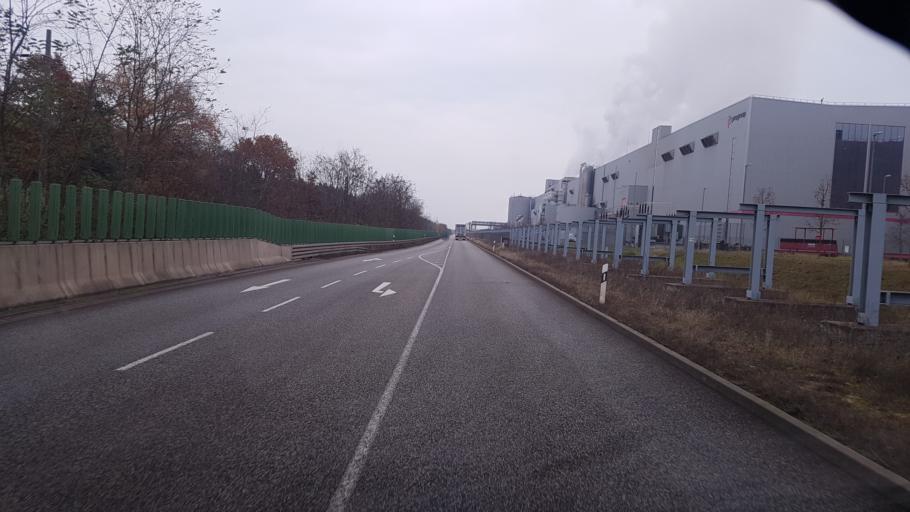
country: DE
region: Brandenburg
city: Ziltendorf
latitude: 52.1822
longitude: 14.6331
